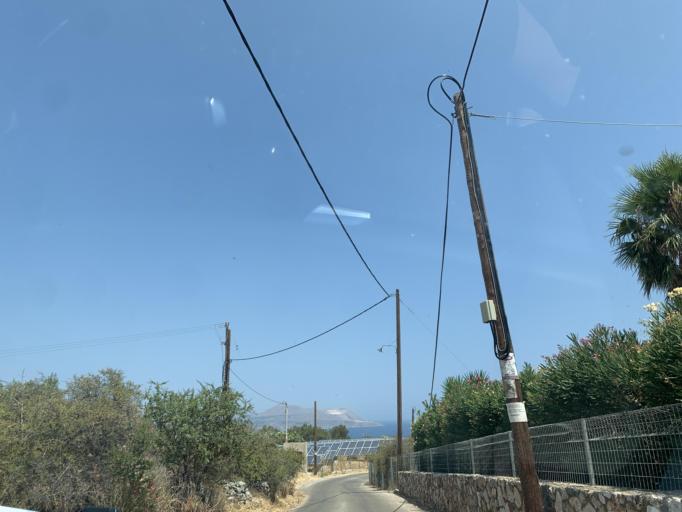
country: GR
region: Crete
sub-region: Nomos Chanias
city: Kalivai
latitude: 35.4502
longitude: 24.2275
